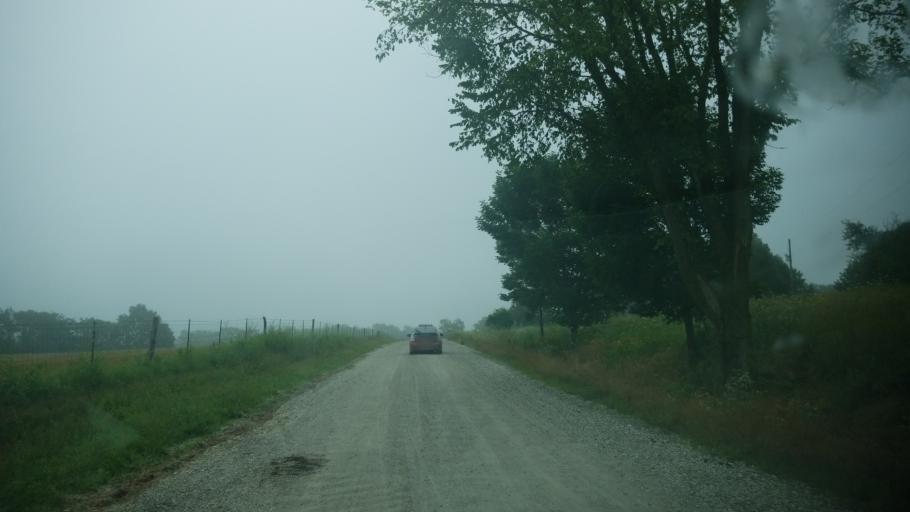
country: US
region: Missouri
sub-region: Audrain County
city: Vandalia
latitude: 39.3092
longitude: -91.3449
